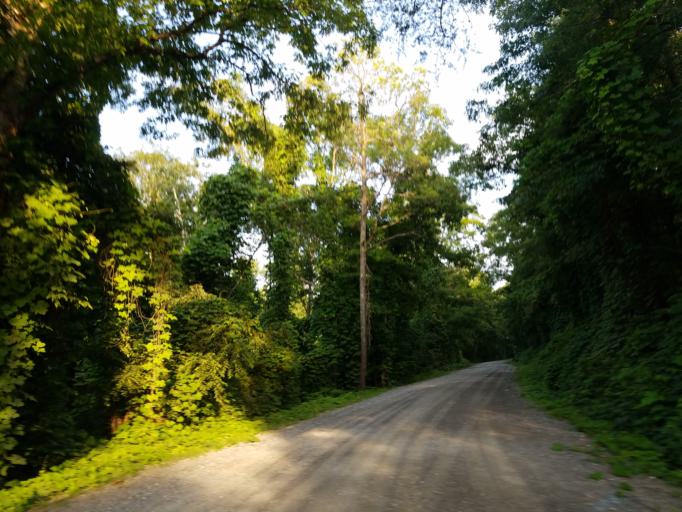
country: US
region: Georgia
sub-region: Pickens County
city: Jasper
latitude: 34.5116
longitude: -84.4283
